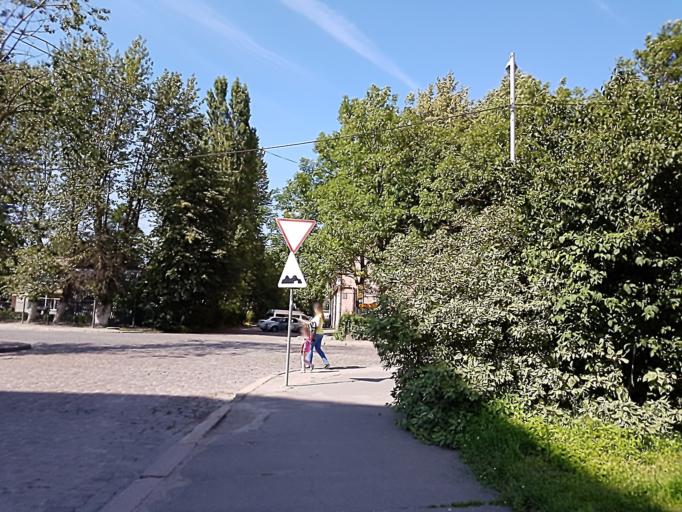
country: RU
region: Kaliningrad
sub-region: Gorod Kaliningrad
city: Kaliningrad
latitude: 54.7011
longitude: 20.5116
